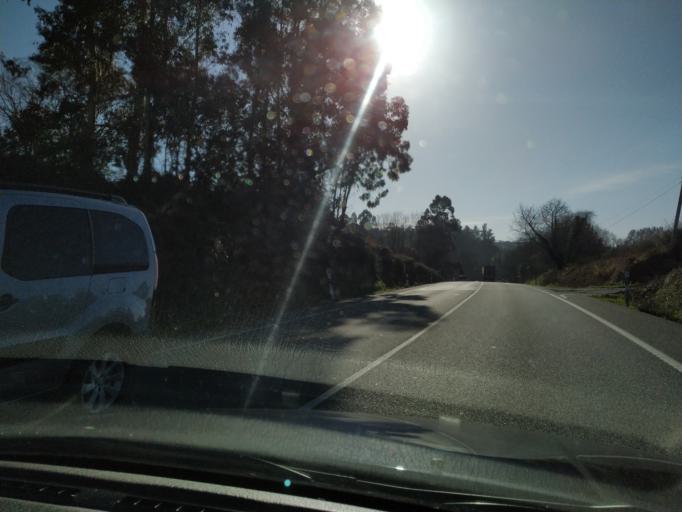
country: ES
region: Galicia
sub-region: Provincia da Coruna
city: Vedra
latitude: 42.8086
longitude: -8.4790
